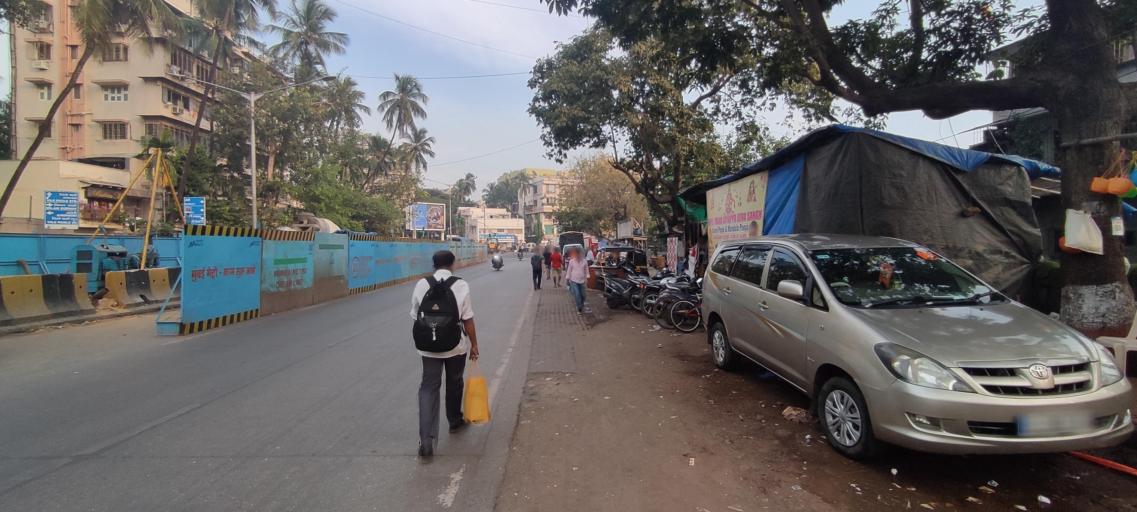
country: IN
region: Maharashtra
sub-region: Mumbai Suburban
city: Mumbai
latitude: 19.1018
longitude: 72.8383
